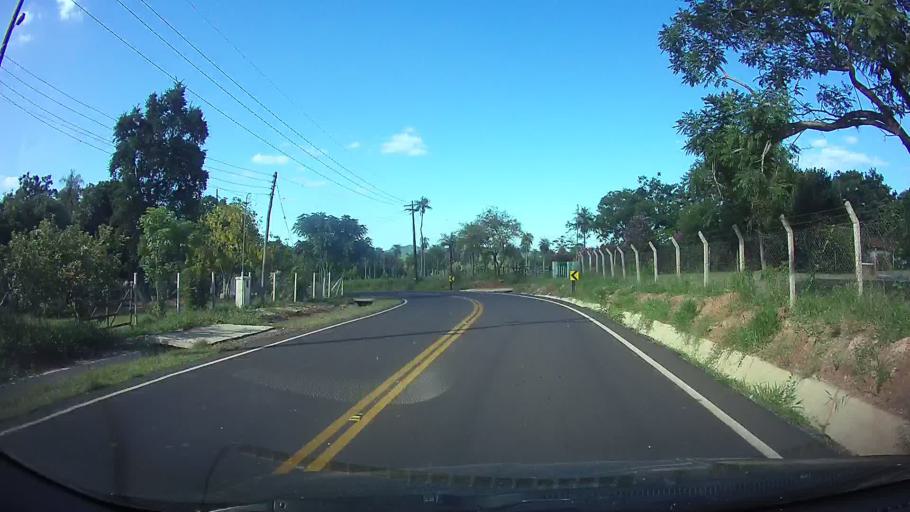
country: PY
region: Cordillera
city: Caacupe
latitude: -25.3595
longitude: -57.1467
